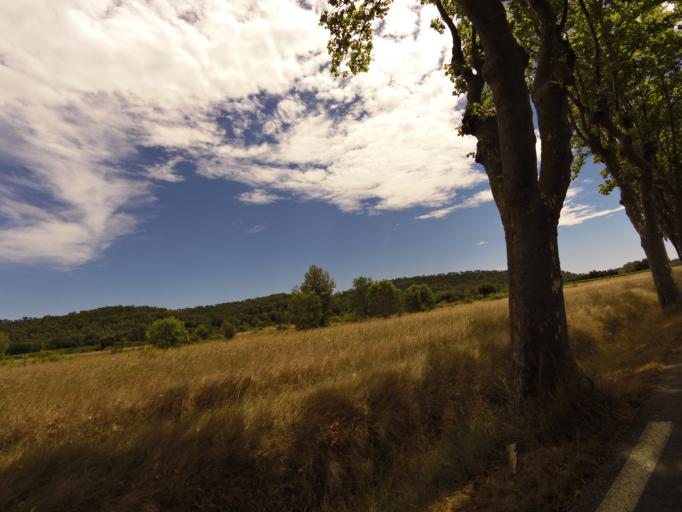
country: FR
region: Languedoc-Roussillon
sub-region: Departement du Gard
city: Quissac
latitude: 43.8536
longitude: 4.0174
